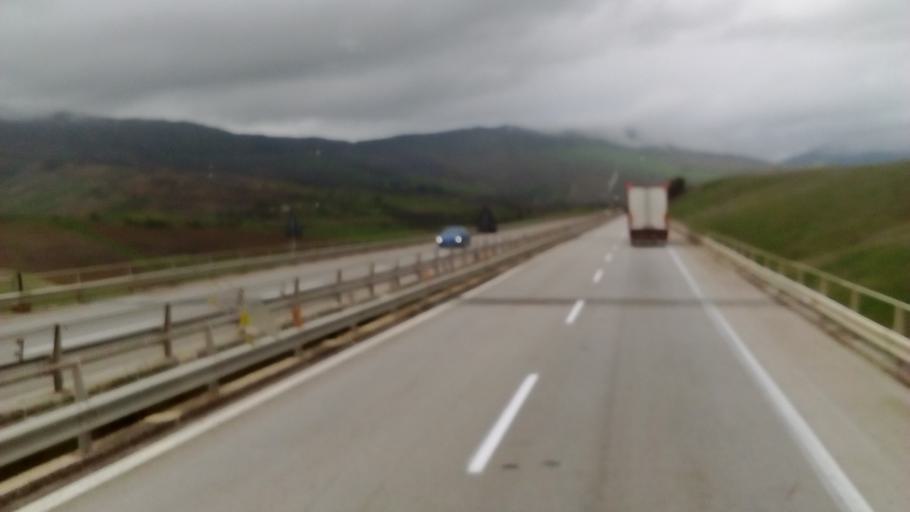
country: IT
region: Sicily
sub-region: Enna
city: Calascibetta
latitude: 37.5761
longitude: 14.2366
